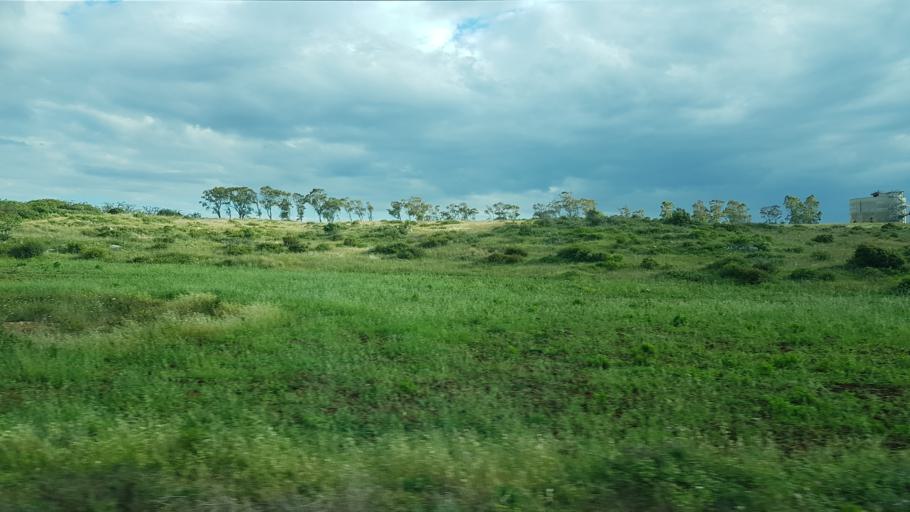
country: IT
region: Apulia
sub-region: Provincia di Brindisi
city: San Vito dei Normanni
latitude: 40.7188
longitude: 17.7495
